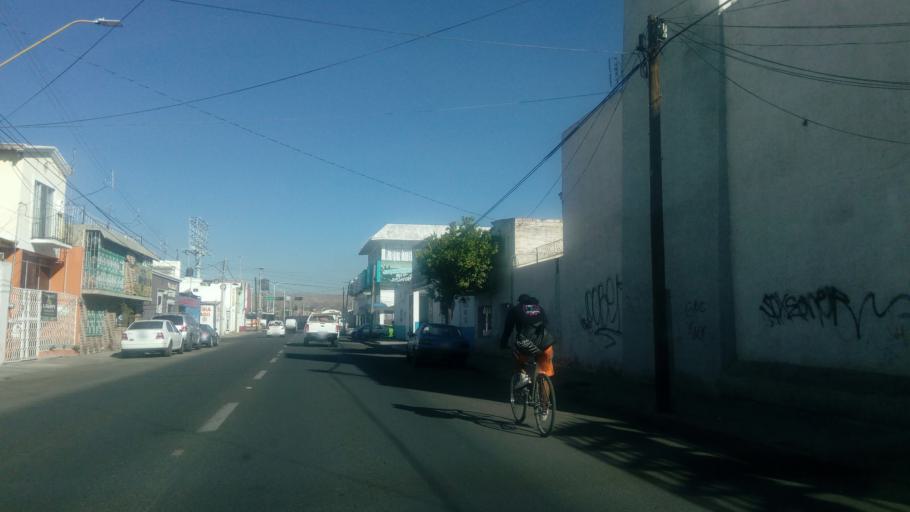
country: MX
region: Durango
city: Victoria de Durango
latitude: 24.0344
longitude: -104.6597
